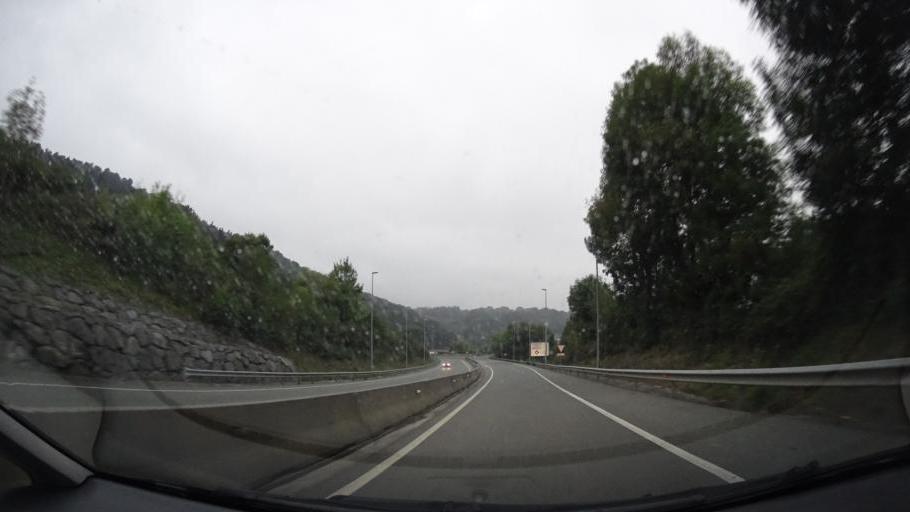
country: ES
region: Basque Country
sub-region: Bizkaia
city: Durango
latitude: 43.1661
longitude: -2.6382
